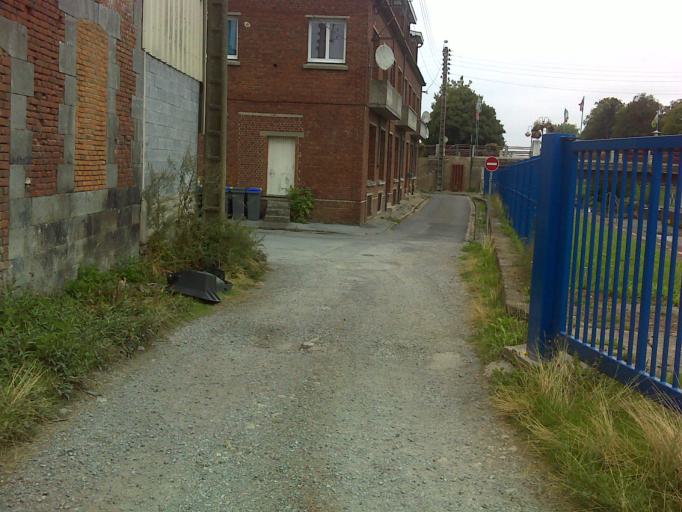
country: FR
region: Nord-Pas-de-Calais
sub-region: Departement du Nord
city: Landrecies
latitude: 50.1264
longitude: 3.6871
